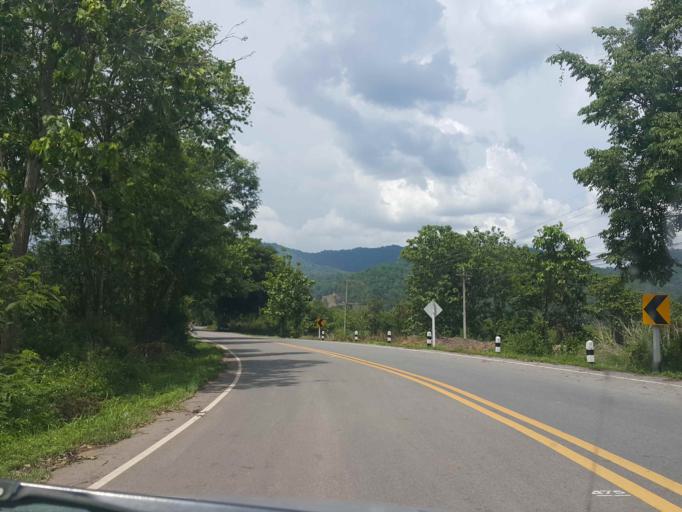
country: TH
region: Nan
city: Ban Luang
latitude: 18.8623
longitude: 100.4633
